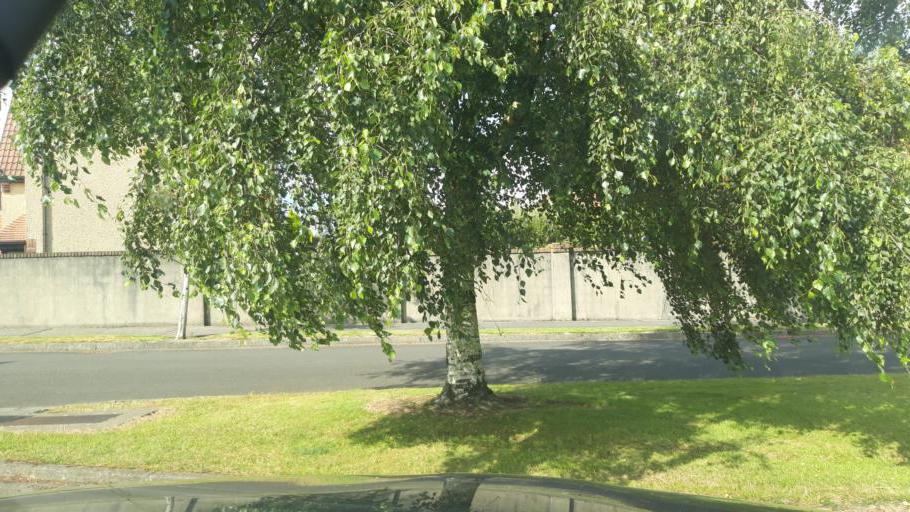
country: IE
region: Munster
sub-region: Waterford
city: Waterford
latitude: 52.2466
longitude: -7.0896
